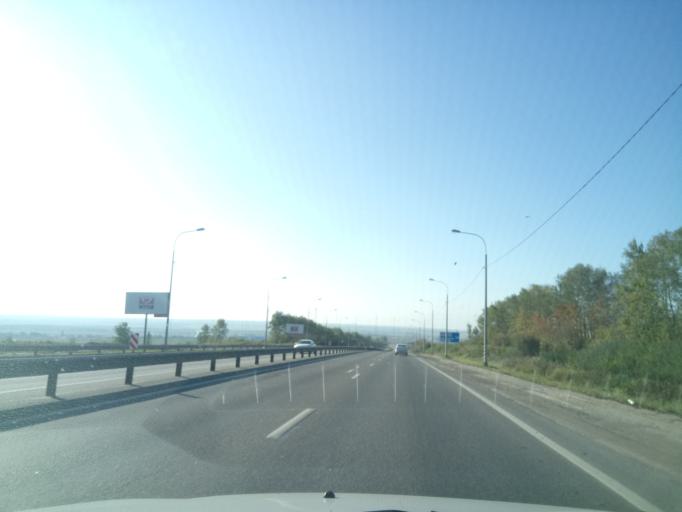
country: RU
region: Nizjnij Novgorod
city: Nizhniy Novgorod
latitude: 56.2042
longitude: 43.9259
